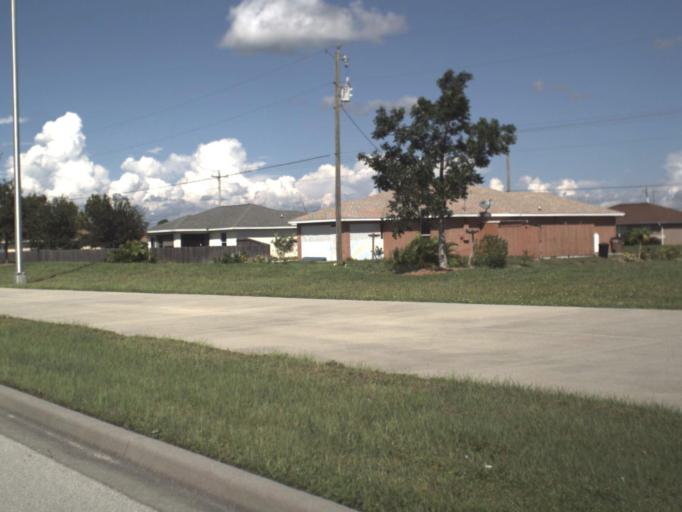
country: US
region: Florida
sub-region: Lee County
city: Lochmoor Waterway Estates
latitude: 26.6764
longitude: -81.9414
